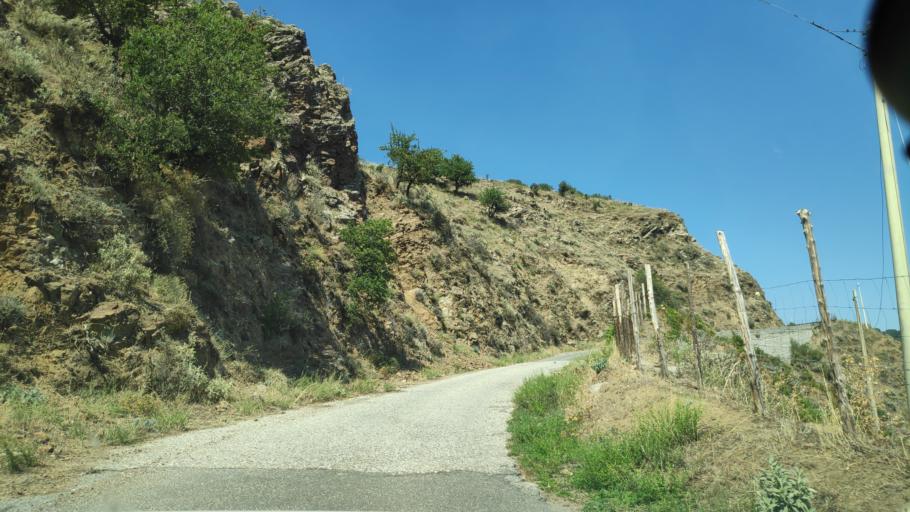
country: IT
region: Calabria
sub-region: Provincia di Reggio Calabria
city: Bova
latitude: 38.0100
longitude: 15.9329
